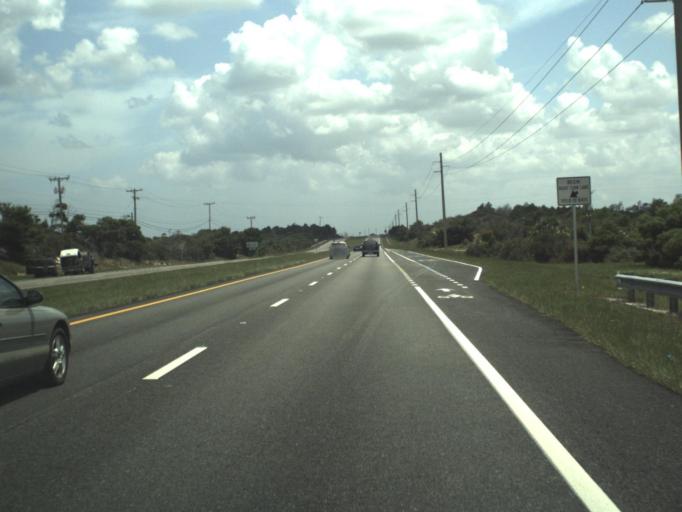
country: US
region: Florida
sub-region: Martin County
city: Hobe Sound
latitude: 27.0366
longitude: -80.1127
